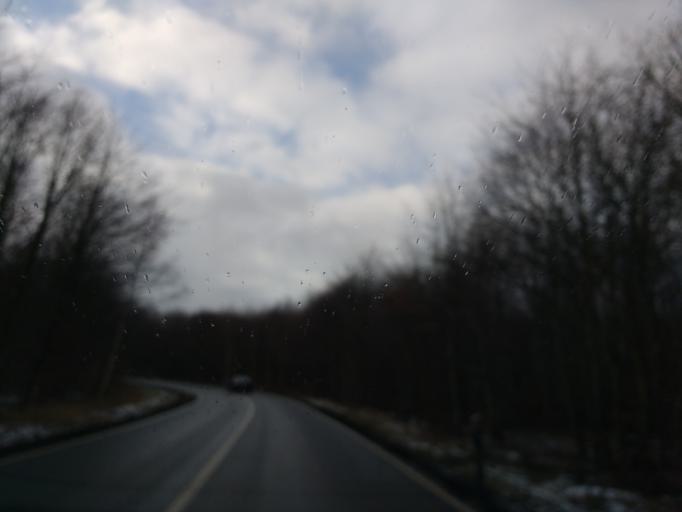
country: DE
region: Saxony-Anhalt
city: Neinstedt
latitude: 51.7108
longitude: 11.0732
